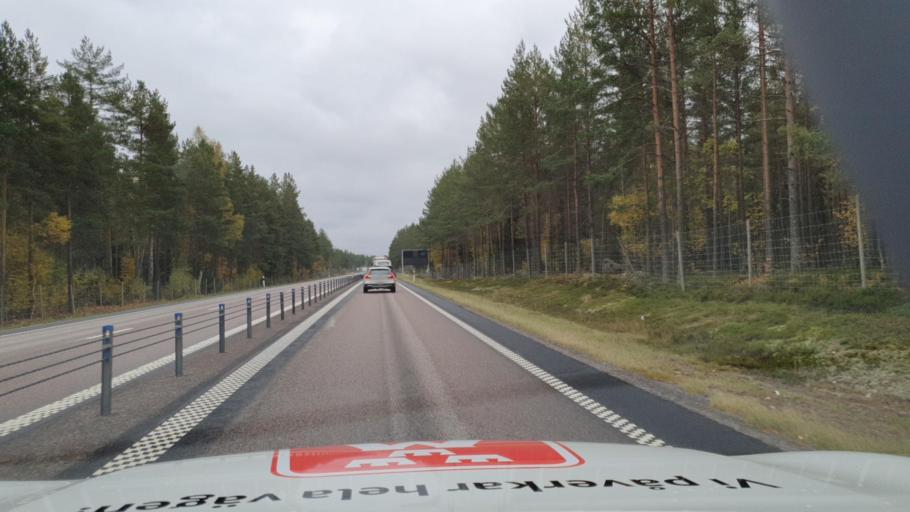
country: SE
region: Gaevleborg
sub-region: Gavle Kommun
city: Norrsundet
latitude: 60.9665
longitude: 17.0248
